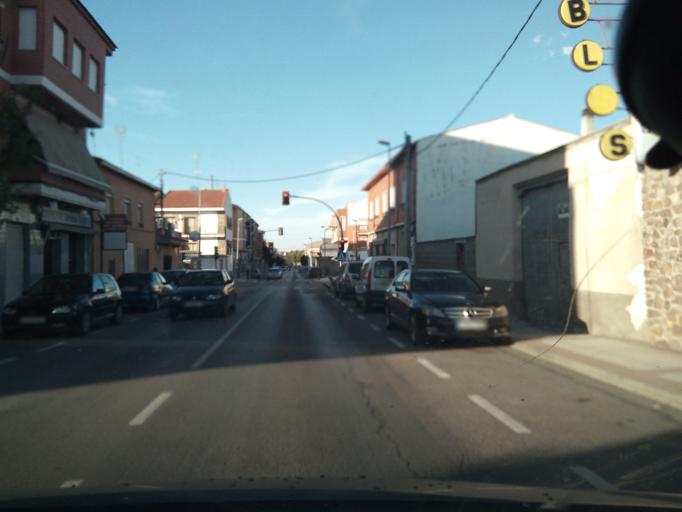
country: ES
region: Castille-La Mancha
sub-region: Province of Toledo
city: Villacanas
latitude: 39.6196
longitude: -3.3354
